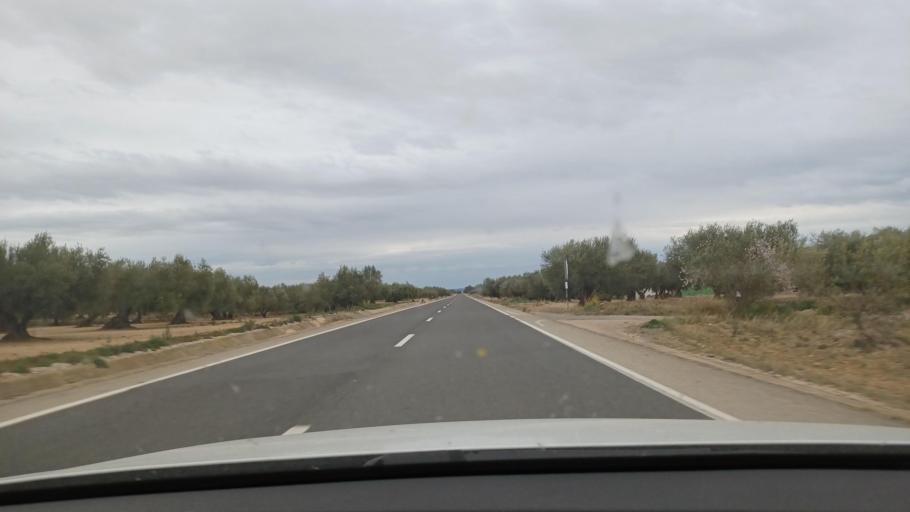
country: ES
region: Catalonia
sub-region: Provincia de Tarragona
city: Ulldecona
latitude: 40.6544
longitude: 0.4012
